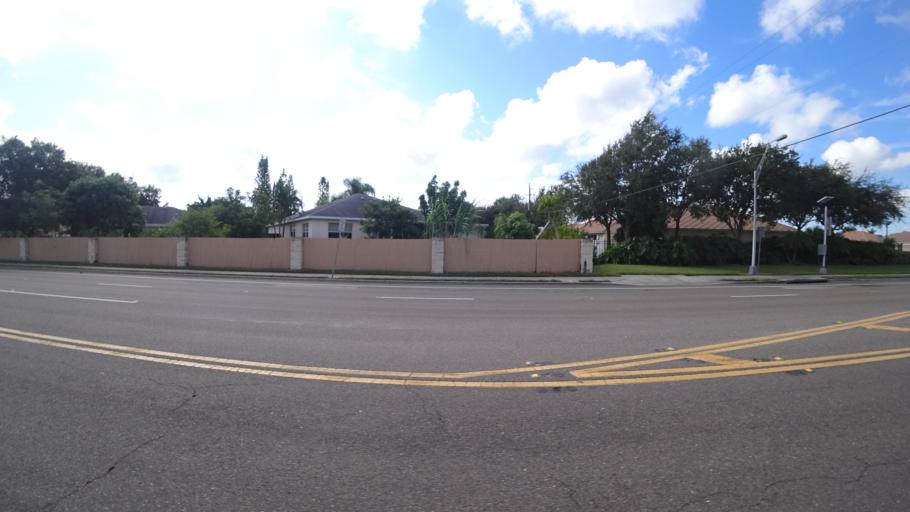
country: US
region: Florida
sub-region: Sarasota County
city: North Sarasota
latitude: 27.4036
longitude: -82.5216
